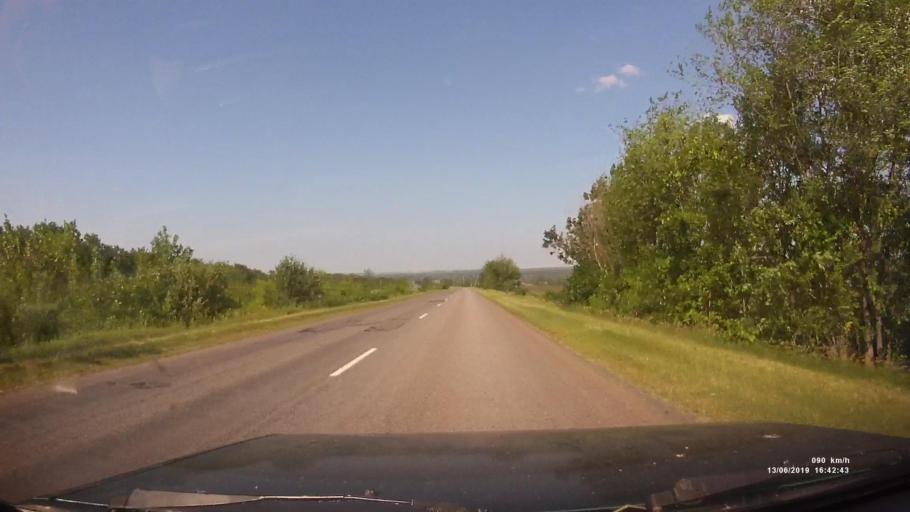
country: RU
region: Rostov
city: Kazanskaya
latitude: 49.9446
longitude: 41.4082
